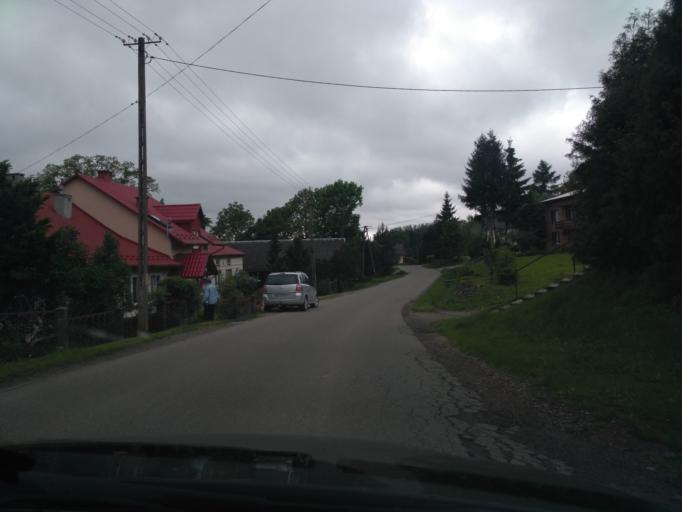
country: PL
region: Subcarpathian Voivodeship
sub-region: Powiat strzyzowski
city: Frysztak
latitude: 49.8032
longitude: 21.5657
